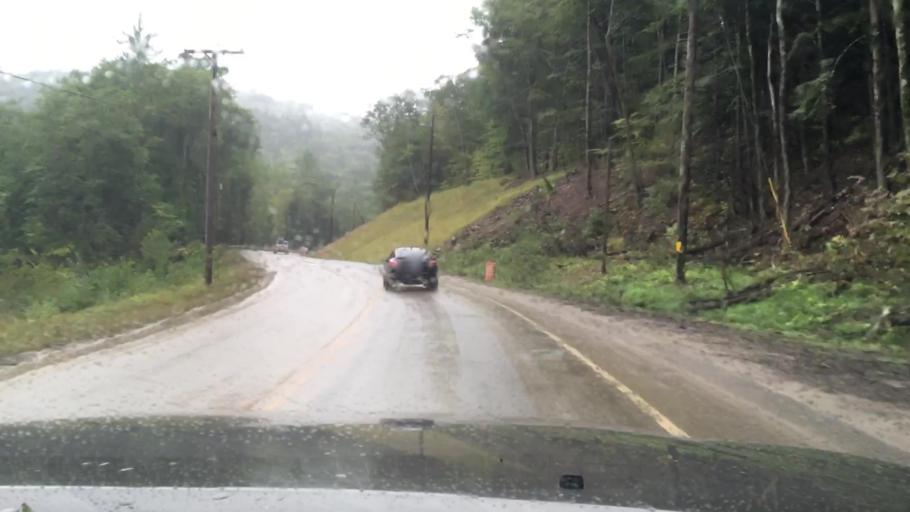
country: US
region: New Hampshire
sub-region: Cheshire County
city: Marlborough
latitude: 42.9779
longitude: -72.2055
